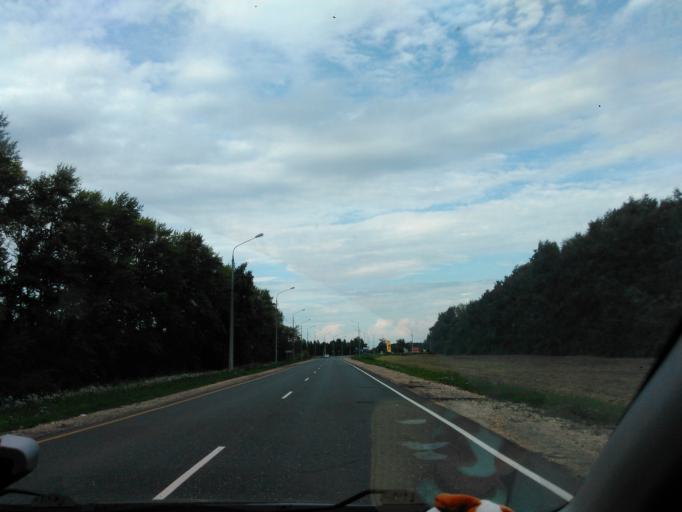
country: RU
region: Penza
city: Lermontovo
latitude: 52.9694
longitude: 43.5851
